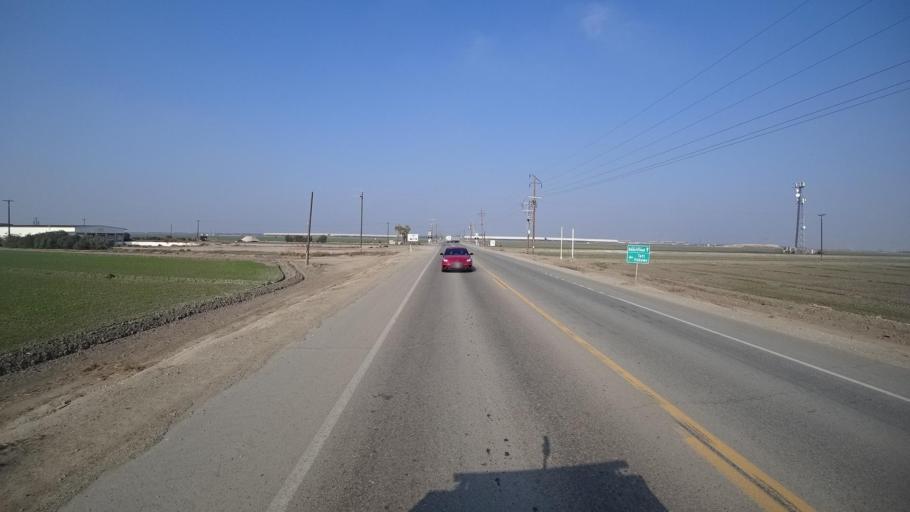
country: US
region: California
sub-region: Kern County
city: Greenfield
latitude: 35.1792
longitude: -119.1100
